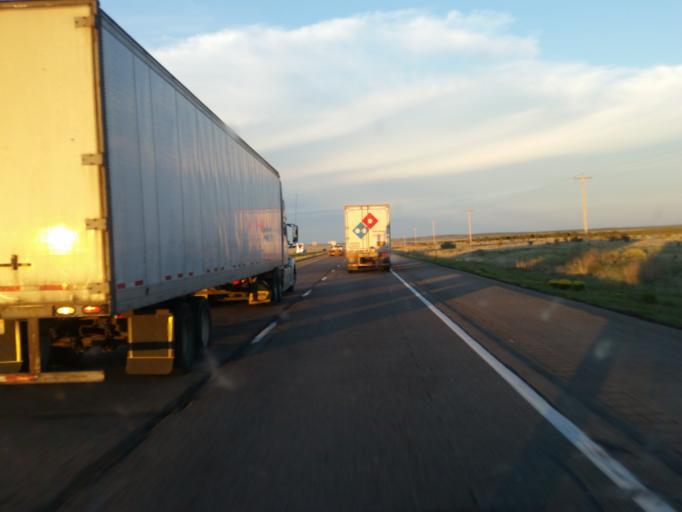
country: US
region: New Mexico
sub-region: San Miguel County
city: Las Vegas
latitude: 34.9931
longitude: -105.3292
